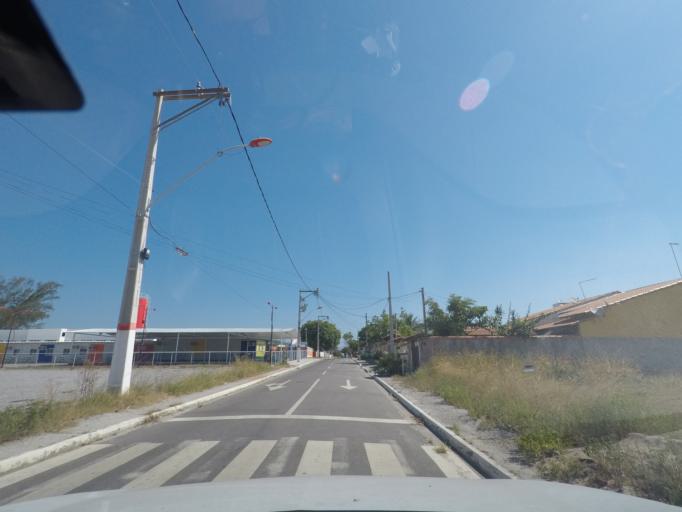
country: BR
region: Rio de Janeiro
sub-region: Niteroi
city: Niteroi
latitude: -22.9629
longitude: -42.9693
